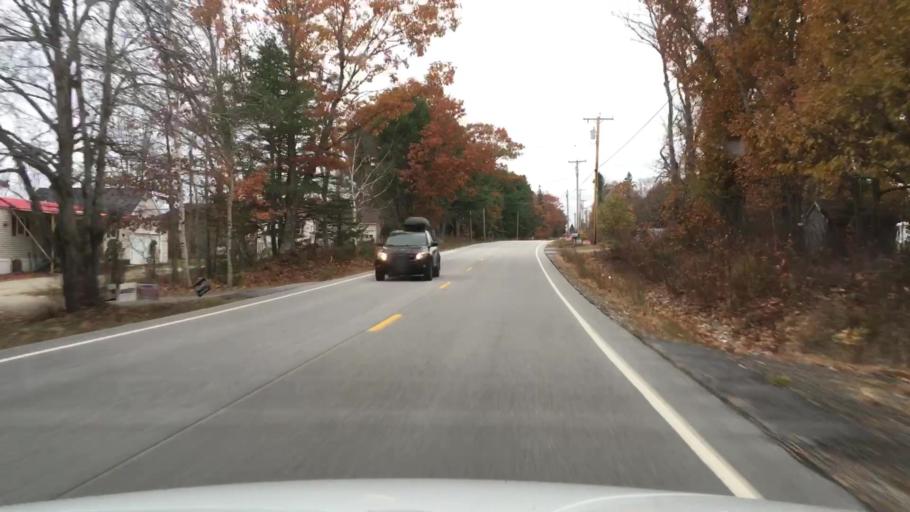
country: US
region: Maine
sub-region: Hancock County
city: Orland
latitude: 44.5414
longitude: -68.6840
